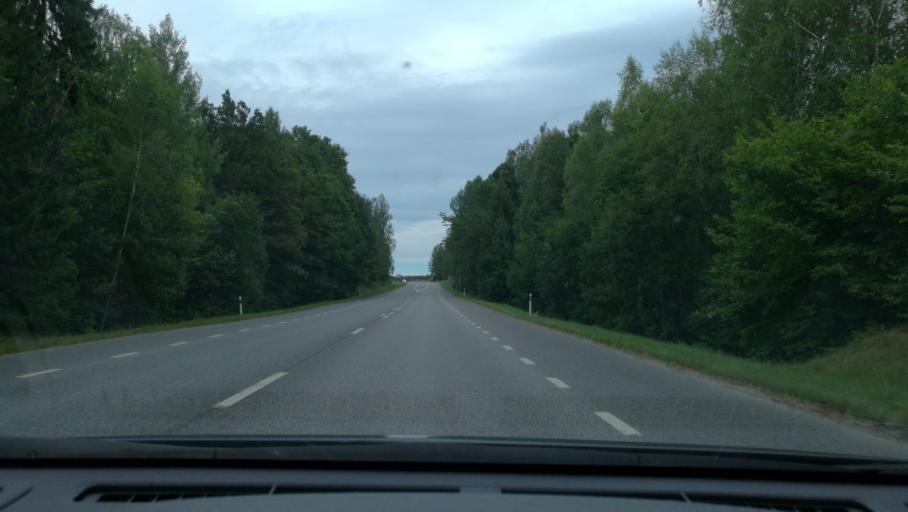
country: SE
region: Soedermanland
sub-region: Katrineholms Kommun
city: Katrineholm
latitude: 58.9738
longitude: 16.2044
